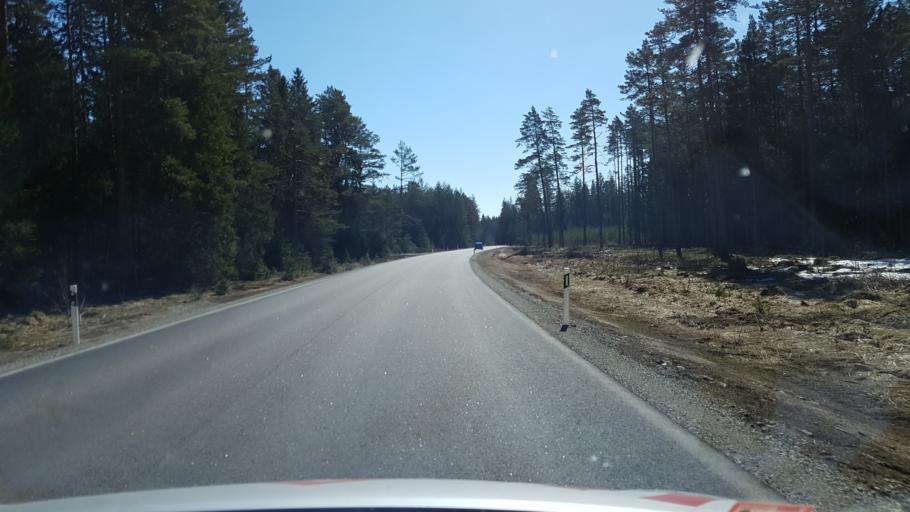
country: EE
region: Laeaene-Virumaa
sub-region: Vinni vald
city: Vinni
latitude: 59.1312
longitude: 26.6060
